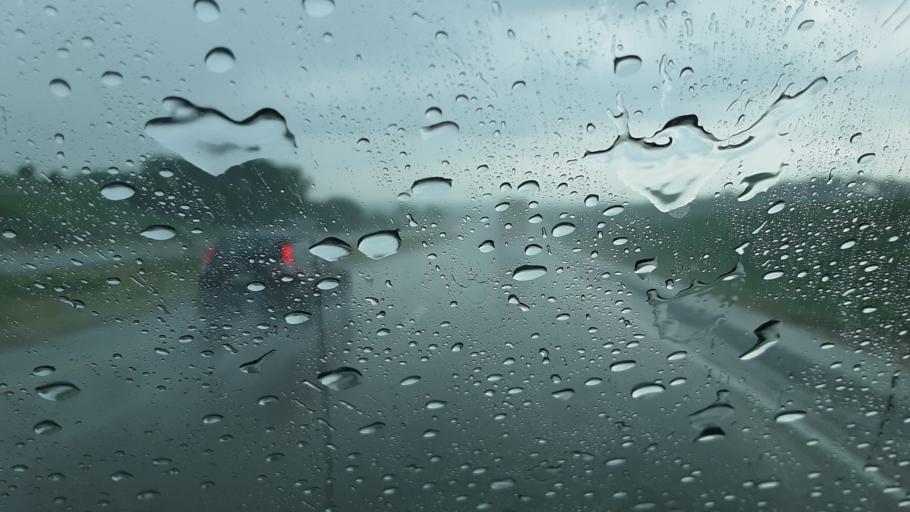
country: US
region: Iowa
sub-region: Pottawattamie County
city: Council Bluffs
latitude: 41.2858
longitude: -95.7808
